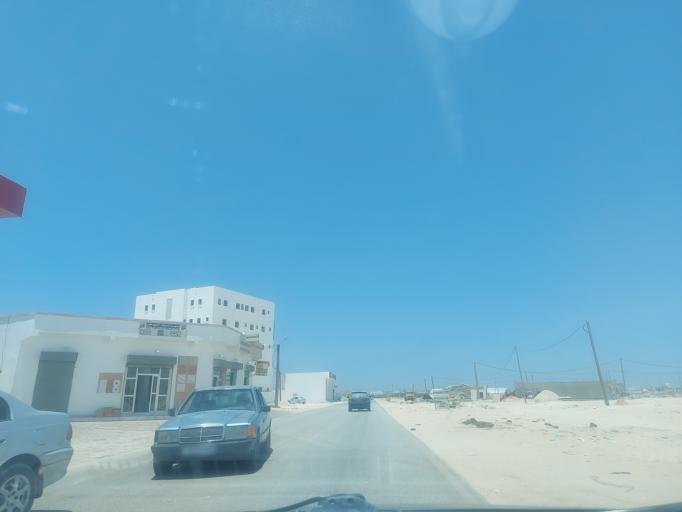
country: MR
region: Nouakchott
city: Nouakchott
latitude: 18.0864
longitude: -15.9524
